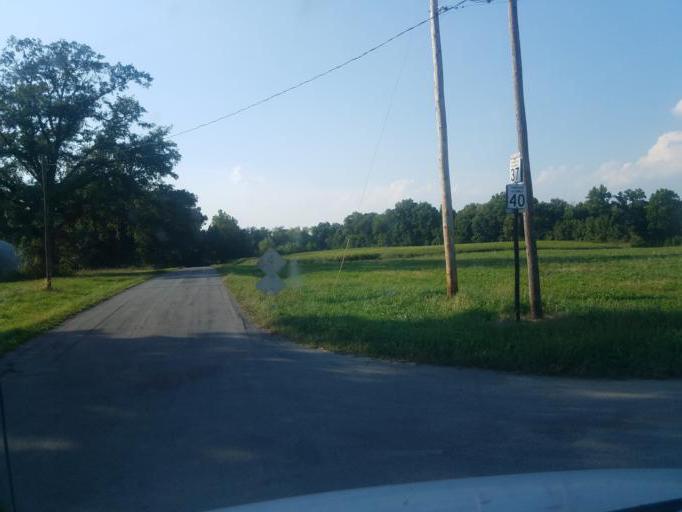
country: US
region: Ohio
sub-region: Wyandot County
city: Upper Sandusky
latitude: 40.9005
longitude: -83.2463
